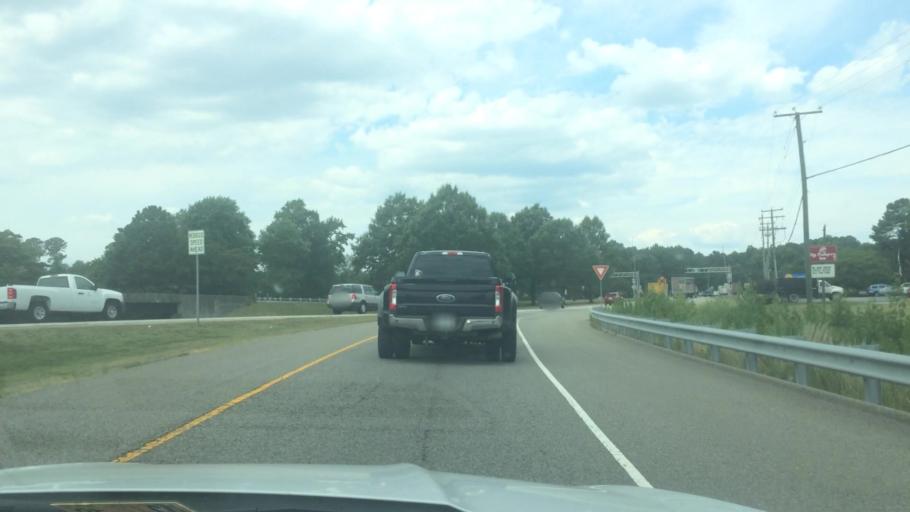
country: US
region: Virginia
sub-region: York County
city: Yorktown
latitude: 37.1735
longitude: -76.5671
